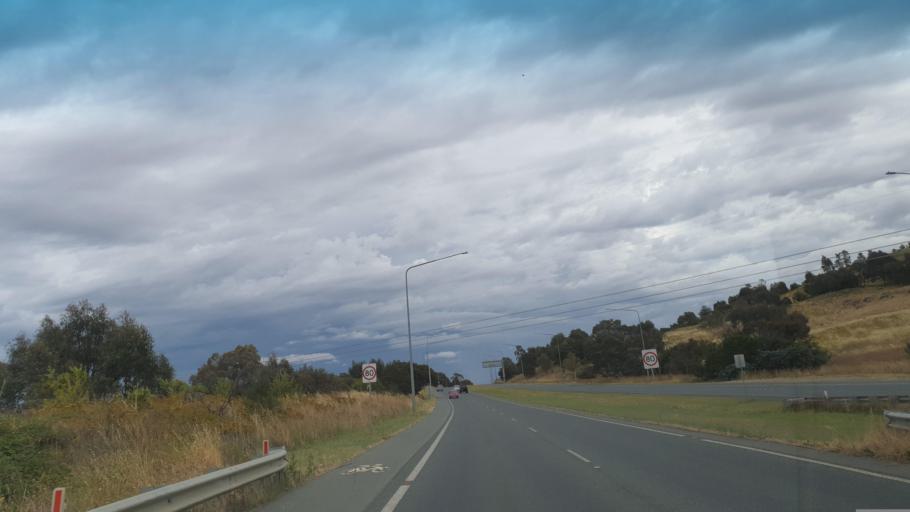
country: AU
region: Australian Capital Territory
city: Macquarie
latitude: -35.2751
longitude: 149.0663
